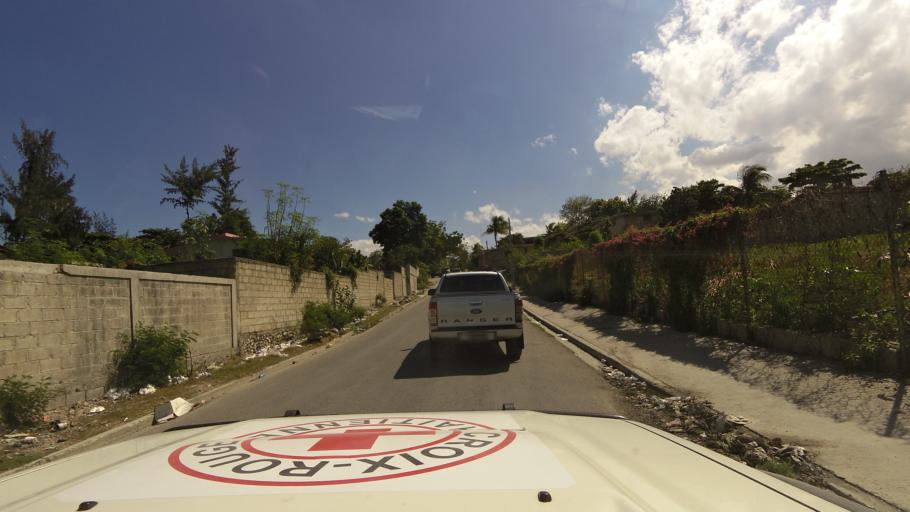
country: HT
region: Ouest
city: Delmas 73
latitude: 18.5694
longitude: -72.3017
